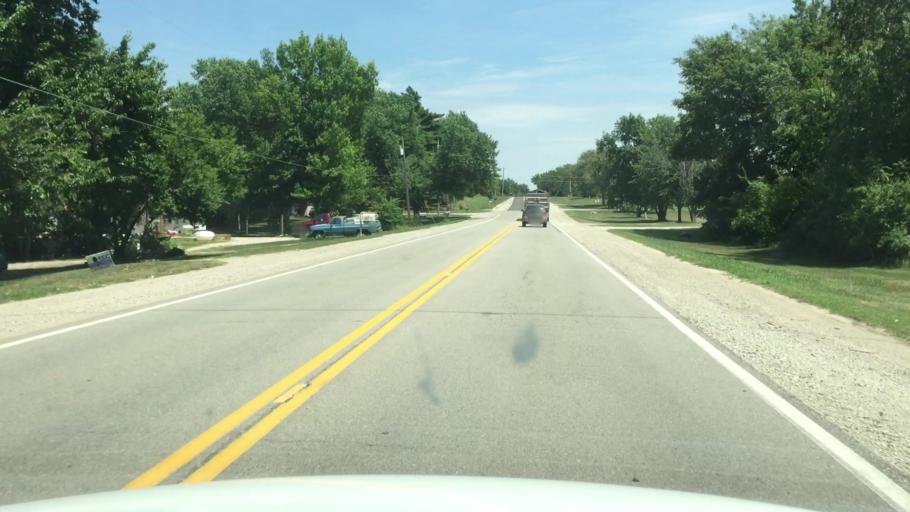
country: US
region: Kansas
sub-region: Shawnee County
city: Topeka
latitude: 38.9861
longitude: -95.5718
